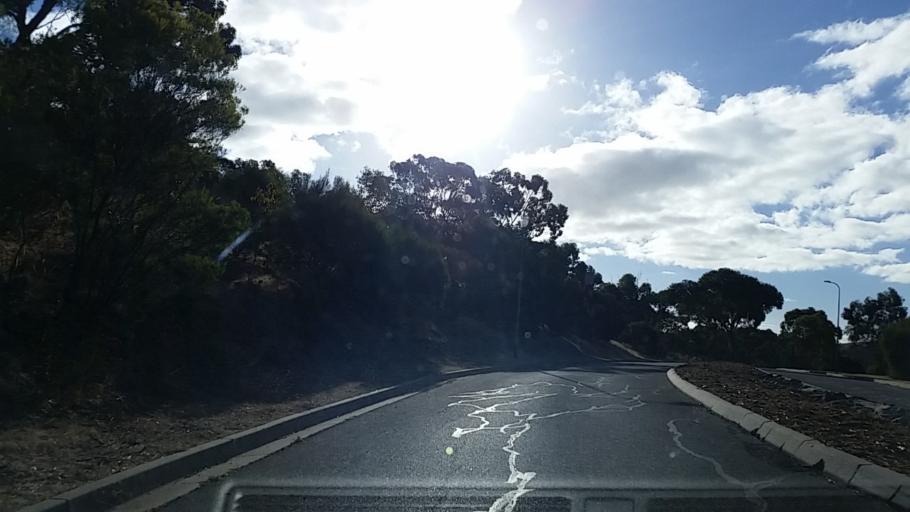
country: AU
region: South Australia
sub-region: Yankalilla
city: Normanville
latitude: -35.5059
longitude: 138.2583
